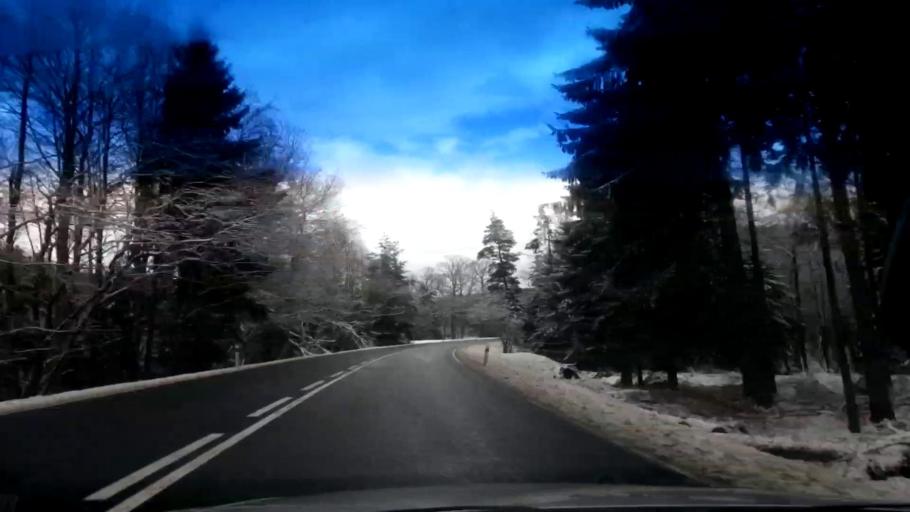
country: CZ
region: Karlovarsky
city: Hazlov
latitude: 50.1886
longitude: 12.2374
